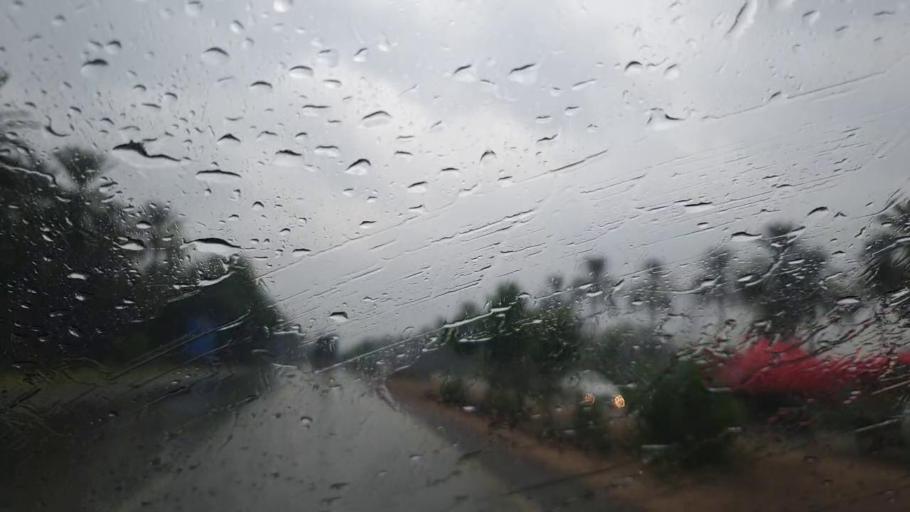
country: PK
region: Sindh
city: Khairpur
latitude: 27.5769
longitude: 68.7538
